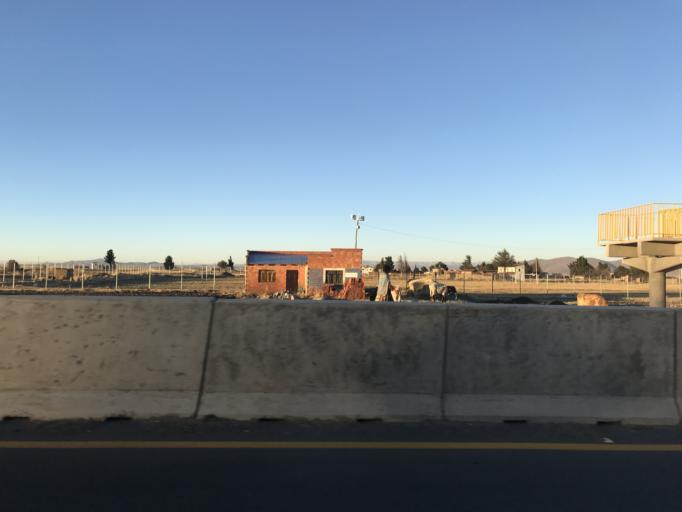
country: BO
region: La Paz
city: Batallas
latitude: -16.2998
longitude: -68.4955
